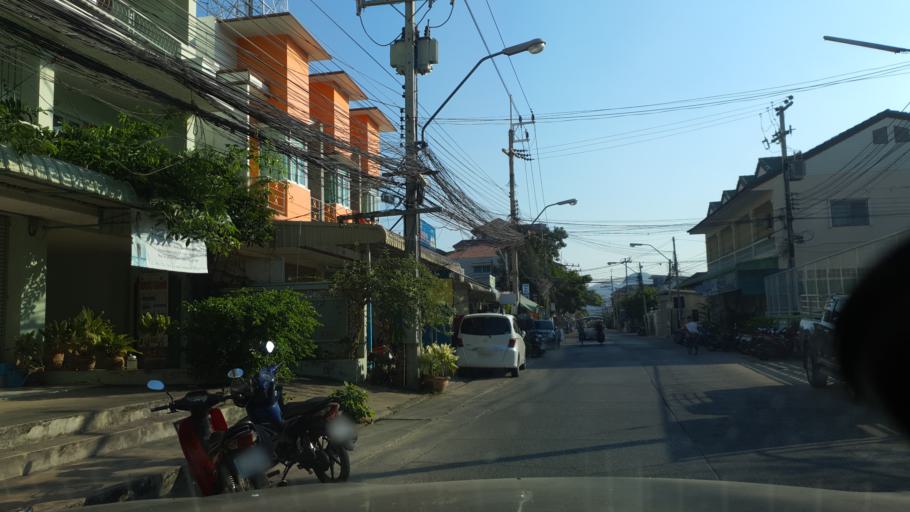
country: TH
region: Prachuap Khiri Khan
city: Hua Hin
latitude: 12.5570
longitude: 99.9527
